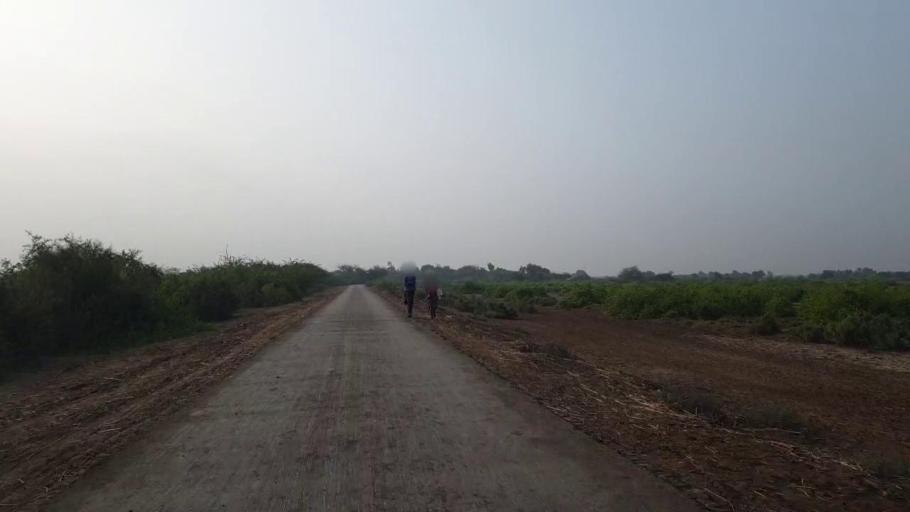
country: PK
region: Sindh
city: Tando Muhammad Khan
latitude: 25.1495
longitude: 68.6058
